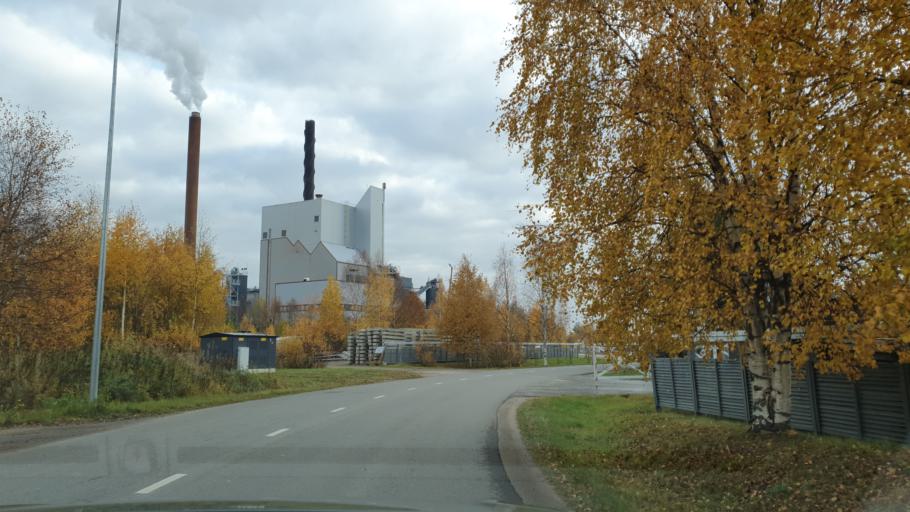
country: FI
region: Lapland
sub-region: Rovaniemi
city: Rovaniemi
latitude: 66.4949
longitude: 25.6706
